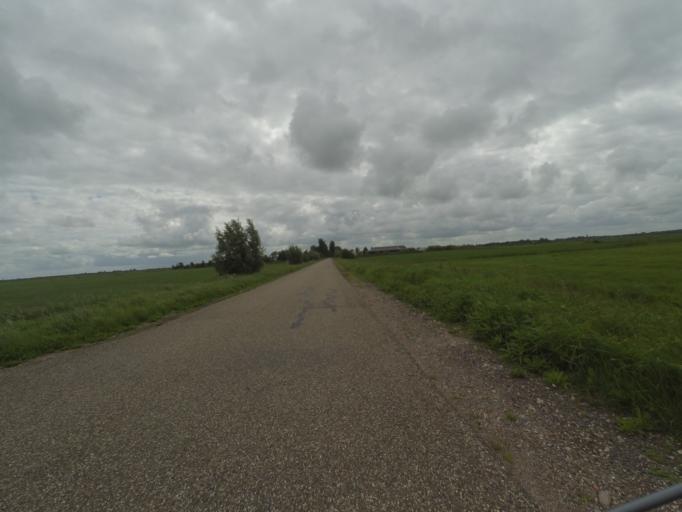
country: NL
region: Friesland
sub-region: Gemeente Kollumerland en Nieuwkruisland
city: Kollumerzwaag
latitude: 53.3109
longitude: 6.0894
